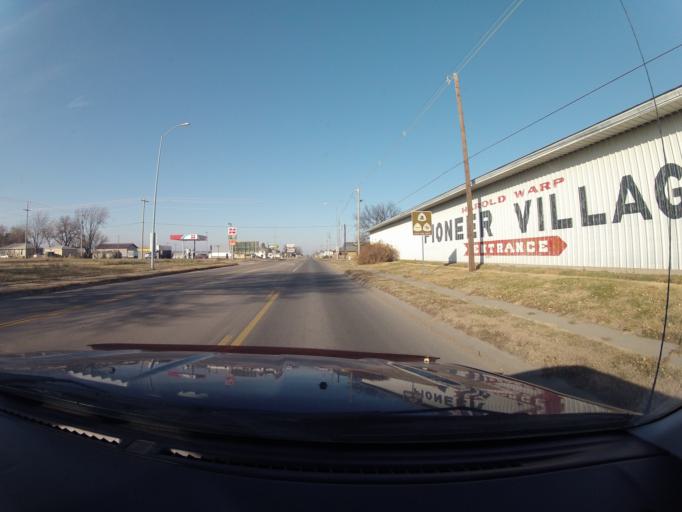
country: US
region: Nebraska
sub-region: Kearney County
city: Minden
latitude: 40.5052
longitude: -98.9518
